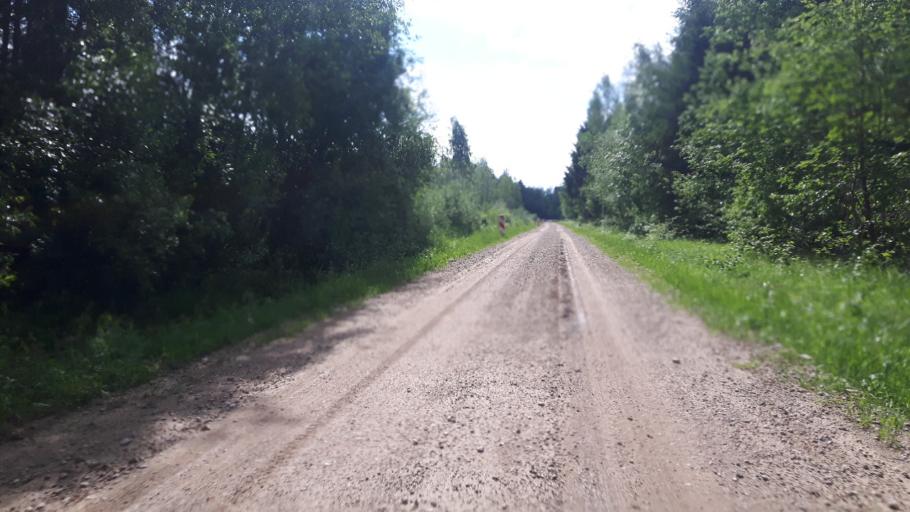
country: EE
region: Paernumaa
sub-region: Vaendra vald (alev)
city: Vandra
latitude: 58.7320
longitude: 25.0064
